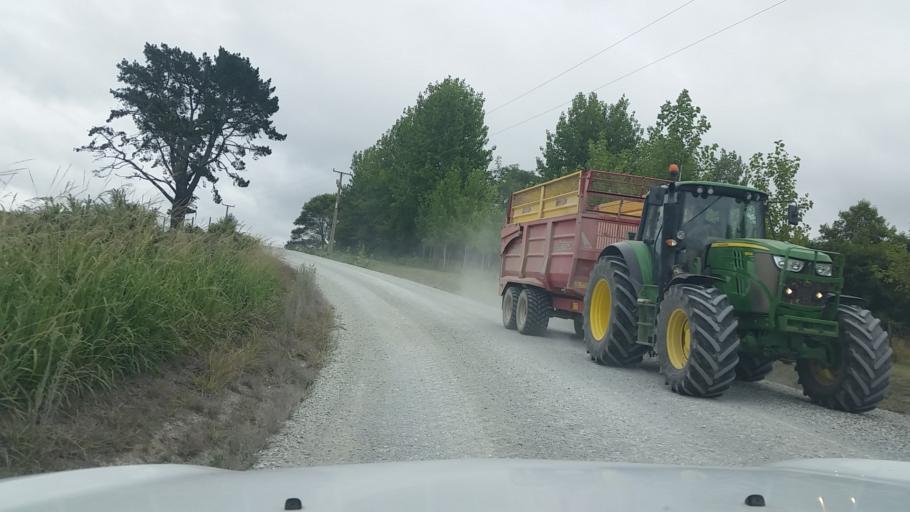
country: NZ
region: Northland
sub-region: Whangarei
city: Maungatapere
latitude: -35.6682
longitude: 174.1645
